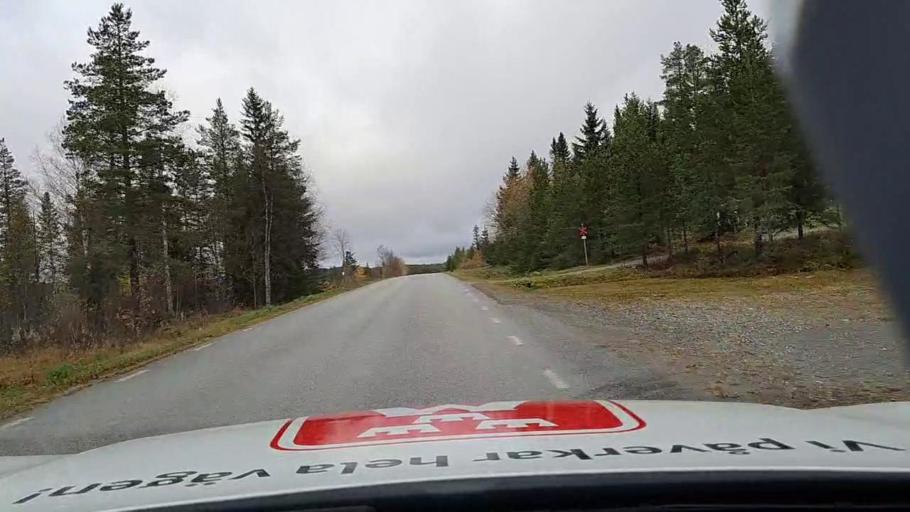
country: SE
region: Jaemtland
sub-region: Bergs Kommun
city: Hoverberg
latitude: 63.0317
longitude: 14.0503
